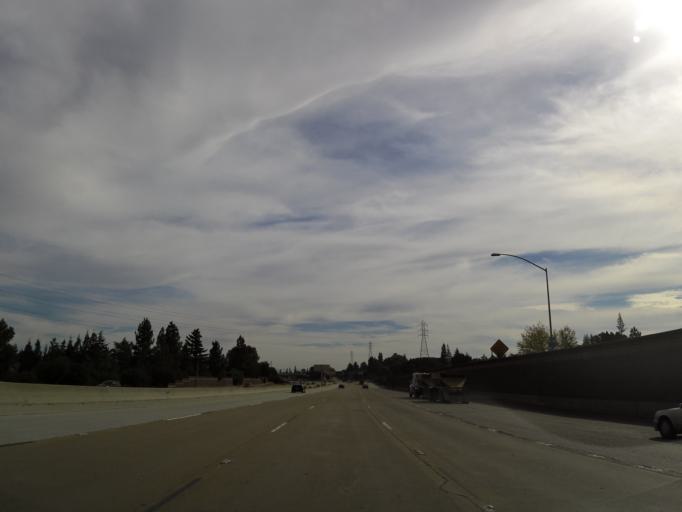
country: US
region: California
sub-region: Santa Clara County
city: Cupertino
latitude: 37.3339
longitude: -122.0648
